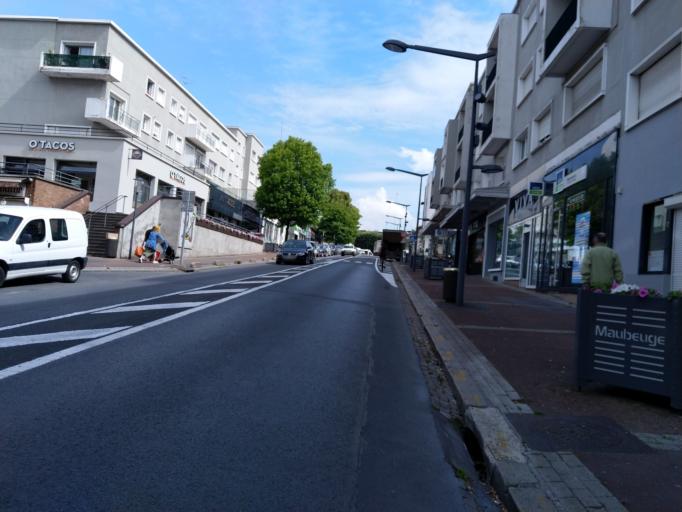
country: FR
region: Nord-Pas-de-Calais
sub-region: Departement du Nord
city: Maubeuge
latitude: 50.2772
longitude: 3.9738
